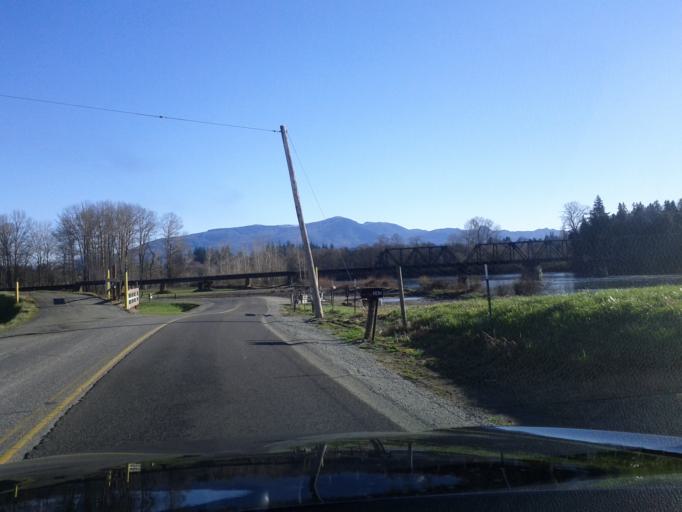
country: US
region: Washington
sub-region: Skagit County
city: Mount Vernon
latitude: 48.4467
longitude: -122.3285
